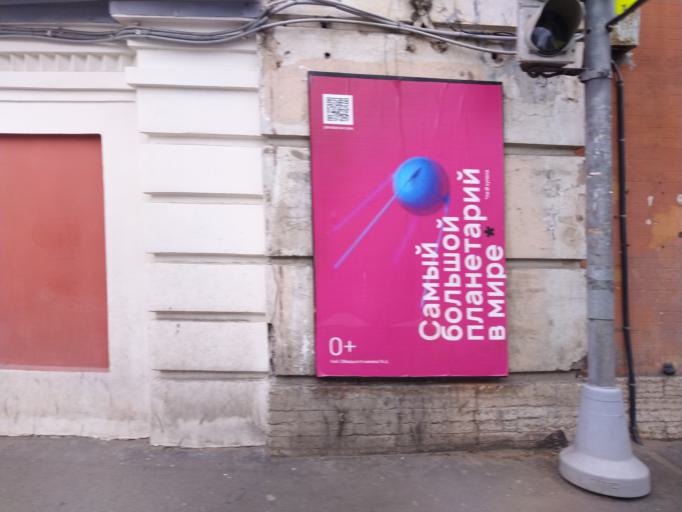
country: RU
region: Leningrad
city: Finlyandskiy
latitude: 59.9561
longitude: 30.3729
